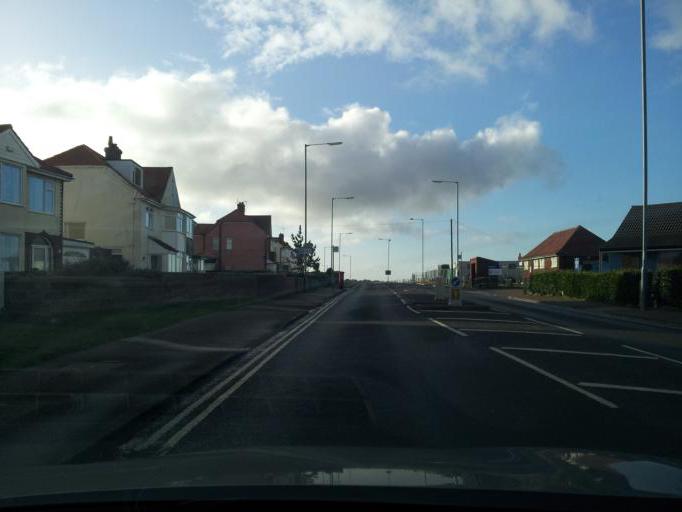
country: GB
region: England
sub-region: Norfolk
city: Cromer
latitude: 52.9332
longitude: 1.2909
